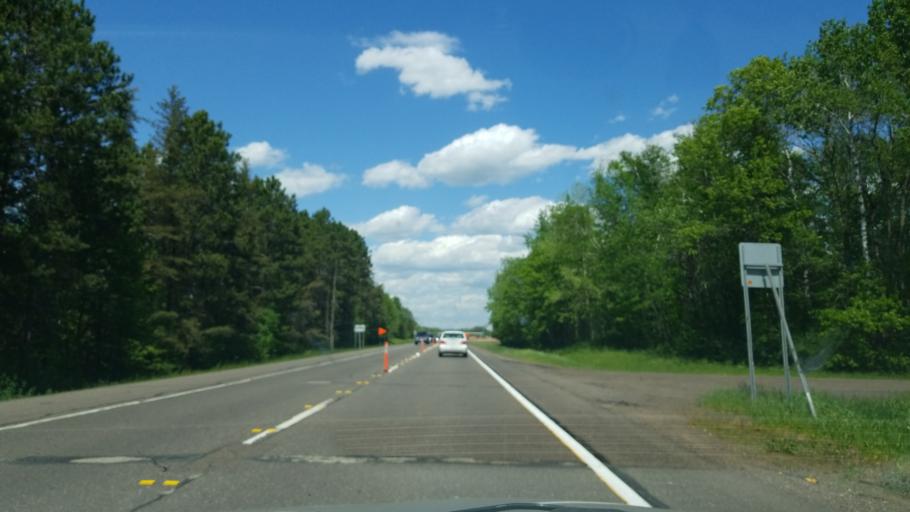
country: US
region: Minnesota
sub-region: Carlton County
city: Moose Lake
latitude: 46.3678
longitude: -92.7965
